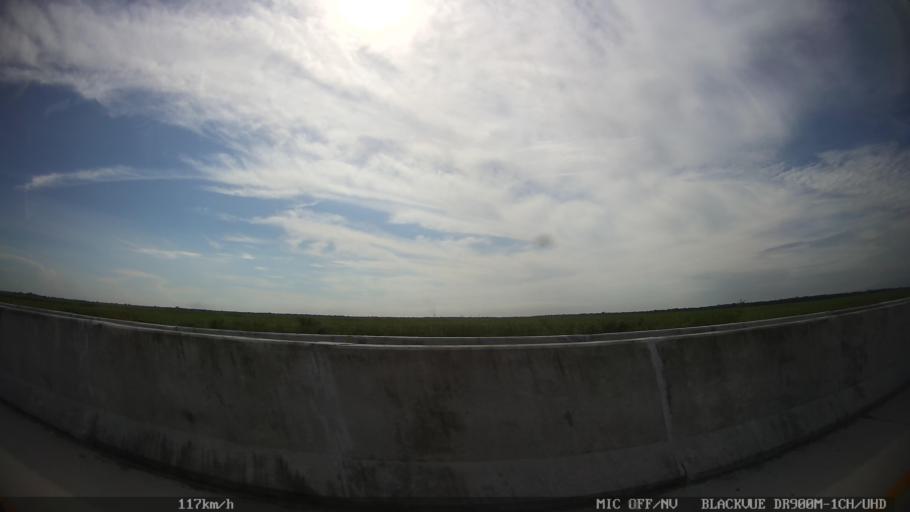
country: ID
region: North Sumatra
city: Binjai
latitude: 3.6670
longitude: 98.5334
